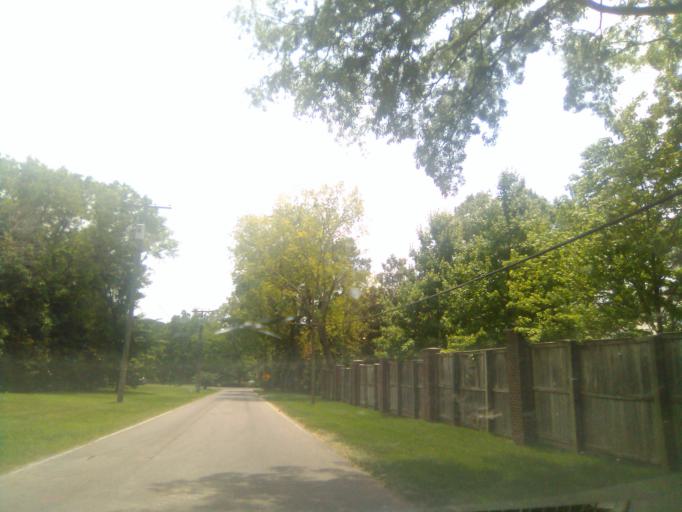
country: US
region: Tennessee
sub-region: Davidson County
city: Belle Meade
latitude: 36.0877
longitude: -86.8532
